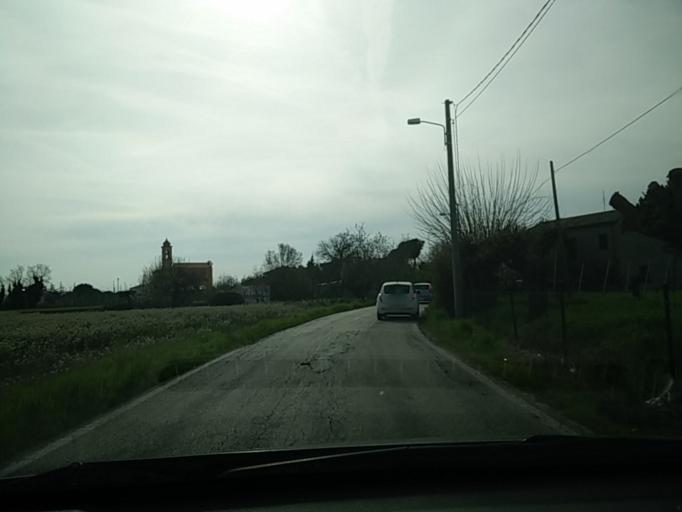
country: IT
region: Emilia-Romagna
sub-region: Provincia di Rimini
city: Santa Giustina
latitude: 44.0733
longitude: 12.5089
